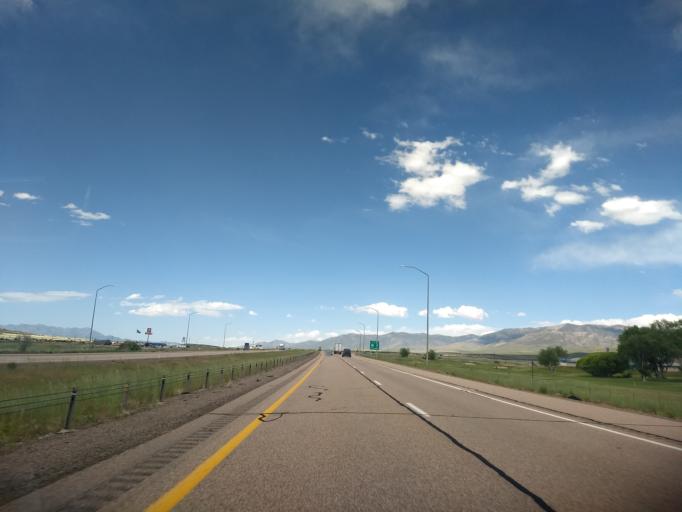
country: US
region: Utah
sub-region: Millard County
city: Fillmore
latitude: 38.9879
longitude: -112.3282
